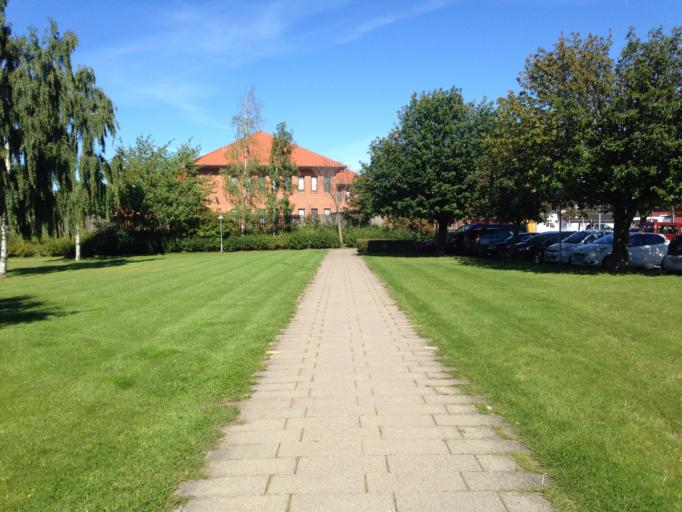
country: DK
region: Capital Region
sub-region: Hvidovre Kommune
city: Hvidovre
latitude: 55.6435
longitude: 12.4776
